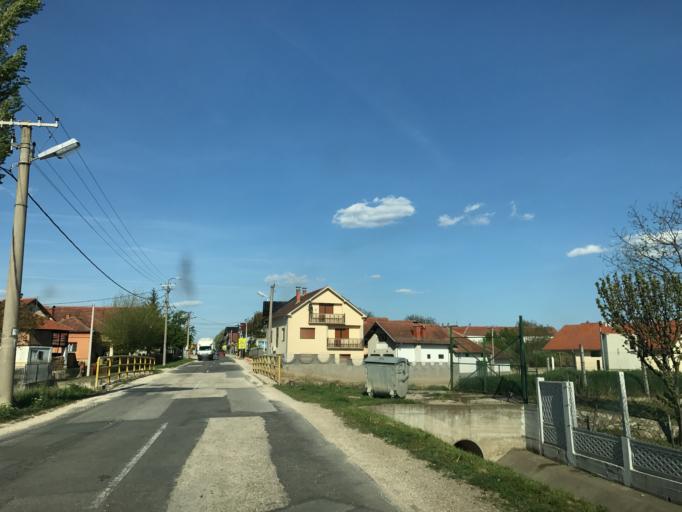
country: RO
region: Mehedinti
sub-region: Comuna Burila Mare
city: Burila Mare
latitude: 44.4933
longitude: 22.4878
